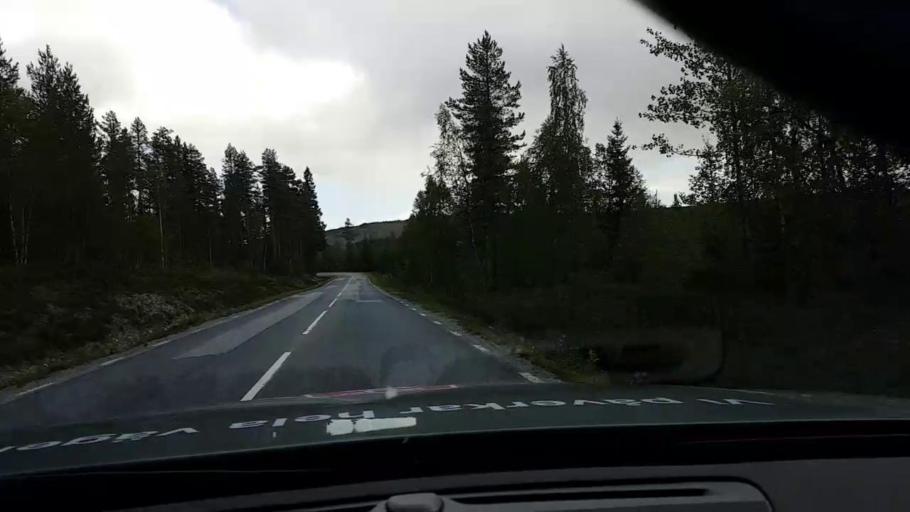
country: SE
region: Vaesterbotten
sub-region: Asele Kommun
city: Asele
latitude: 63.8032
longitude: 17.5475
